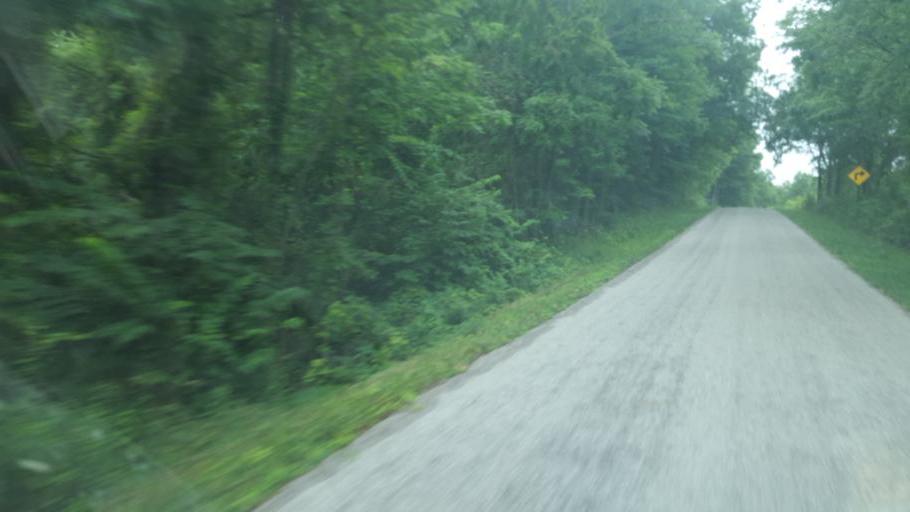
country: US
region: Ohio
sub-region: Knox County
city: Centerburg
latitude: 40.4165
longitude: -82.7196
